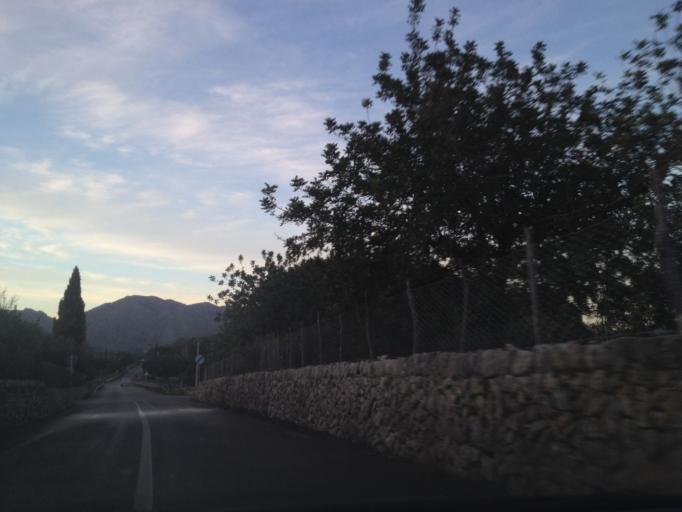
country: ES
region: Balearic Islands
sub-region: Illes Balears
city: Pollenca
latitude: 39.8642
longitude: 3.0438
